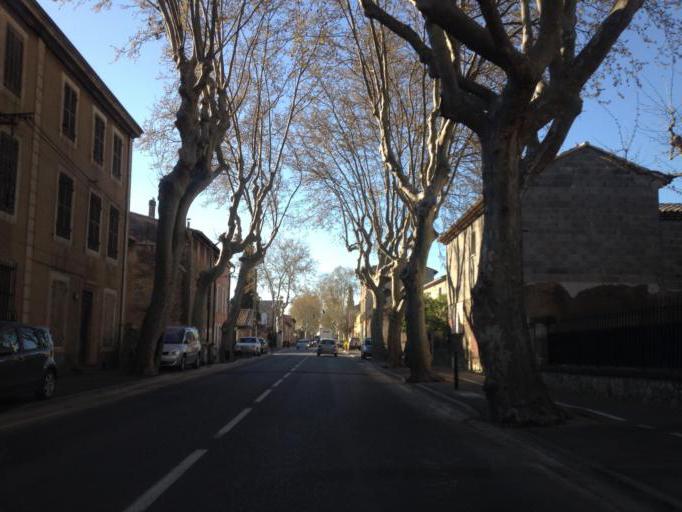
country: FR
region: Provence-Alpes-Cote d'Azur
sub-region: Departement des Bouches-du-Rhone
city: Saint-Cannat
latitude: 43.6221
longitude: 5.2969
